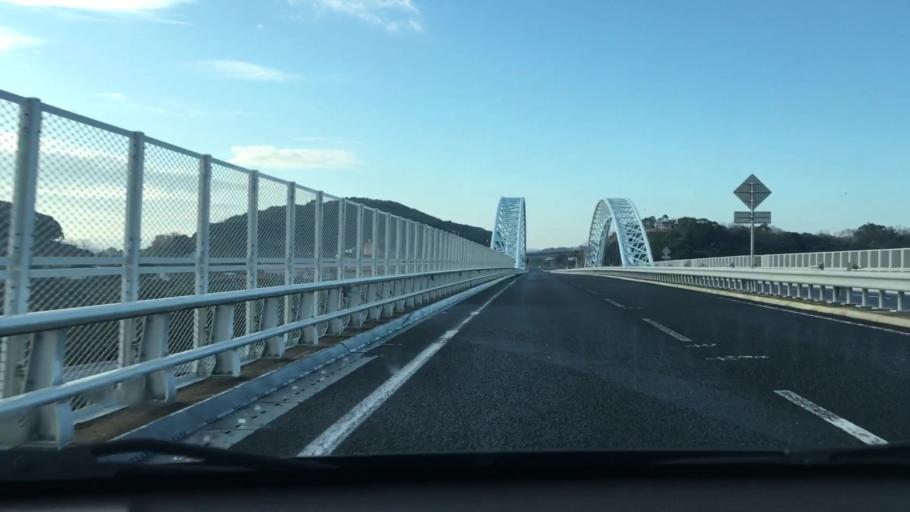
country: JP
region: Nagasaki
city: Sasebo
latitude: 33.0560
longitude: 129.7565
